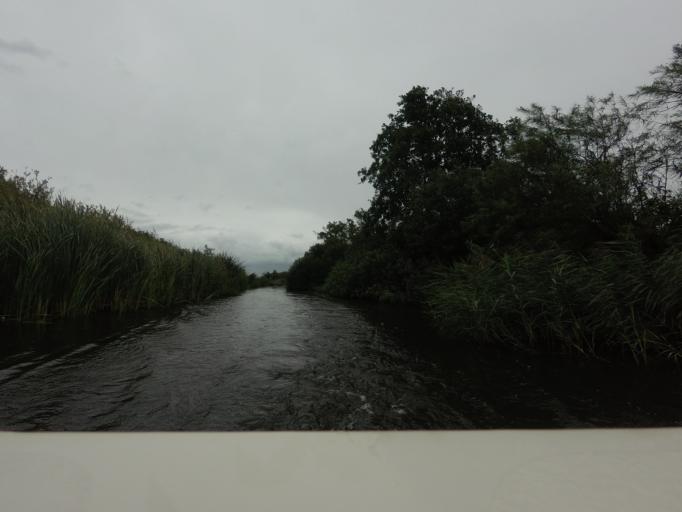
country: NL
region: Friesland
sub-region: Gemeente Boarnsterhim
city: Warten
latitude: 53.1237
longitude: 5.9283
